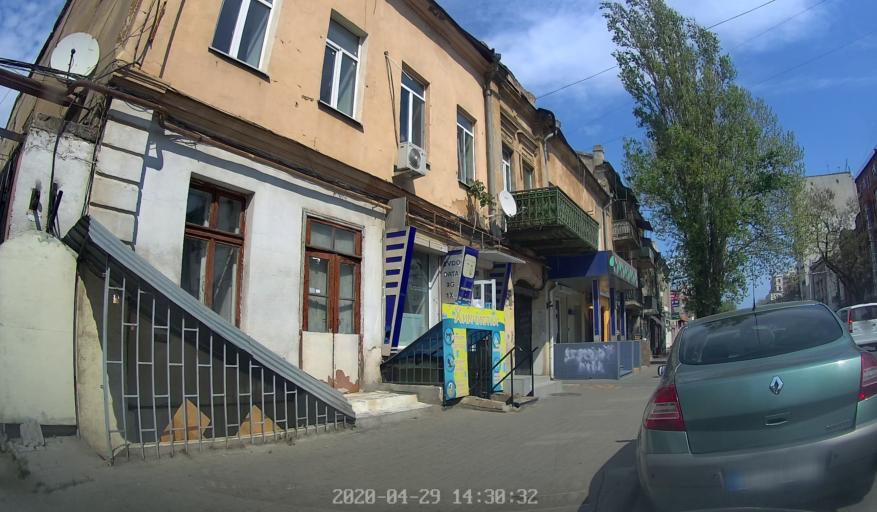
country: GR
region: South Aegean
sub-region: Nomos Kykladon
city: Serifos
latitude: 37.1772
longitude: 24.5882
